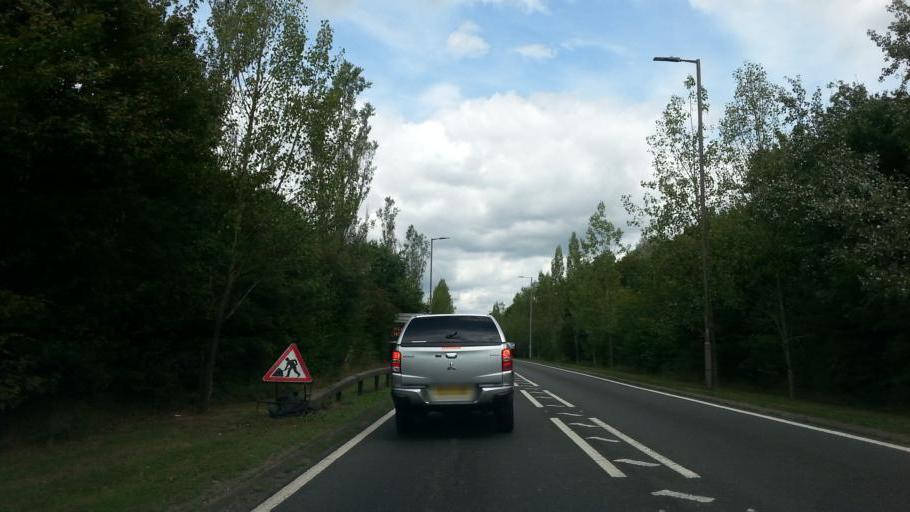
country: GB
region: England
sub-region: Essex
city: South Benfleet
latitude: 51.5615
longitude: 0.5412
